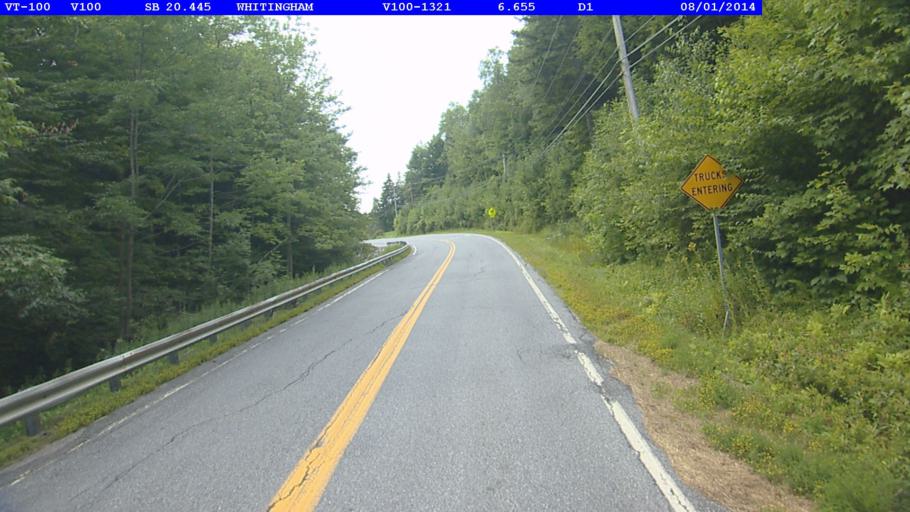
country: US
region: Vermont
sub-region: Windham County
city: Dover
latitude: 42.7888
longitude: -72.8368
